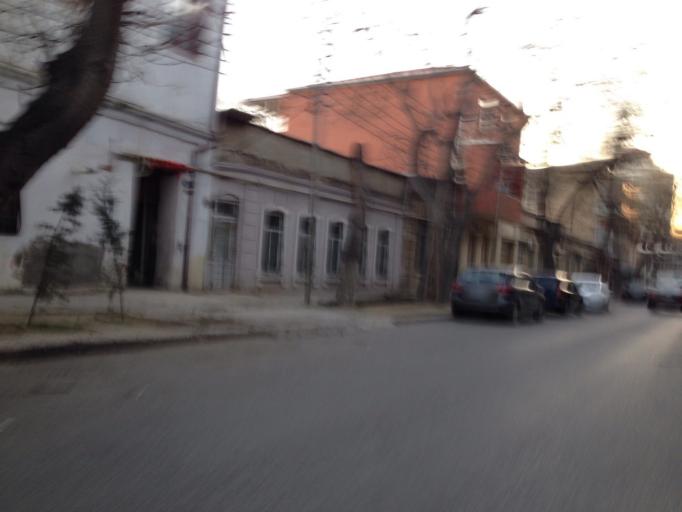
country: AZ
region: Baki
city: Baku
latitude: 40.3877
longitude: 49.8537
